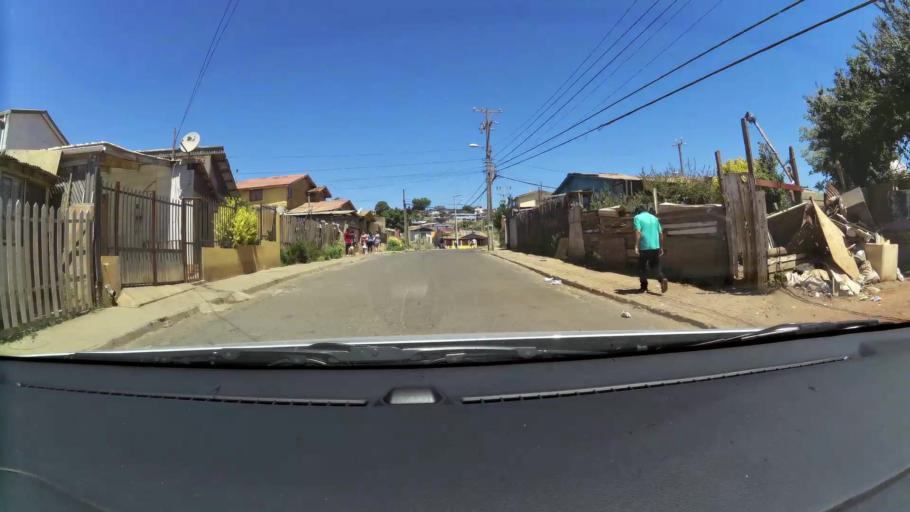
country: CL
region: Valparaiso
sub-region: Provincia de Valparaiso
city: Valparaiso
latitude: -33.0562
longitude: -71.6397
